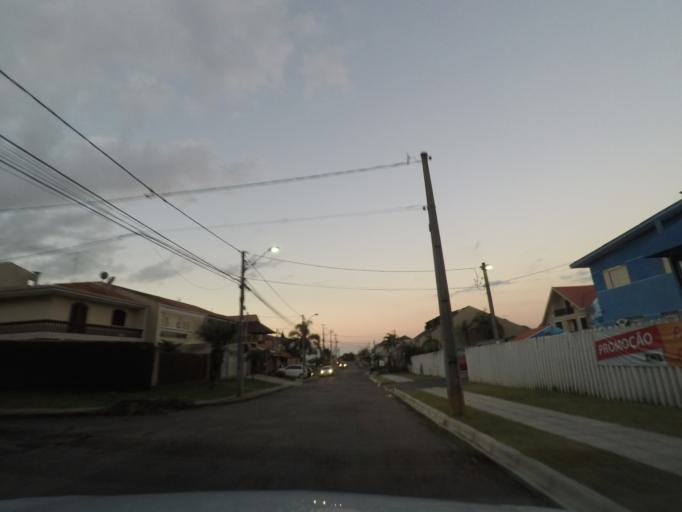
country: BR
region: Parana
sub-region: Sao Jose Dos Pinhais
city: Sao Jose dos Pinhais
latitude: -25.5002
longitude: -49.2650
